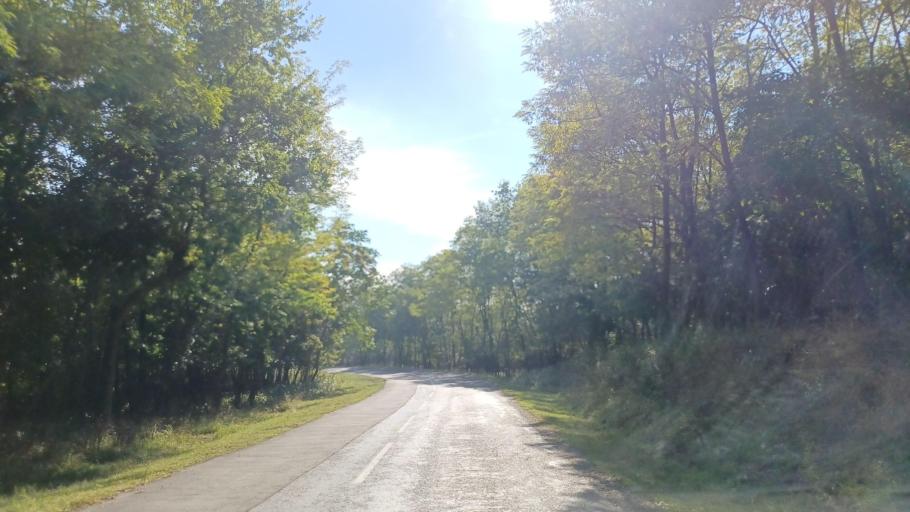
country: HU
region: Tolna
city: Pincehely
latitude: 46.6662
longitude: 18.4800
